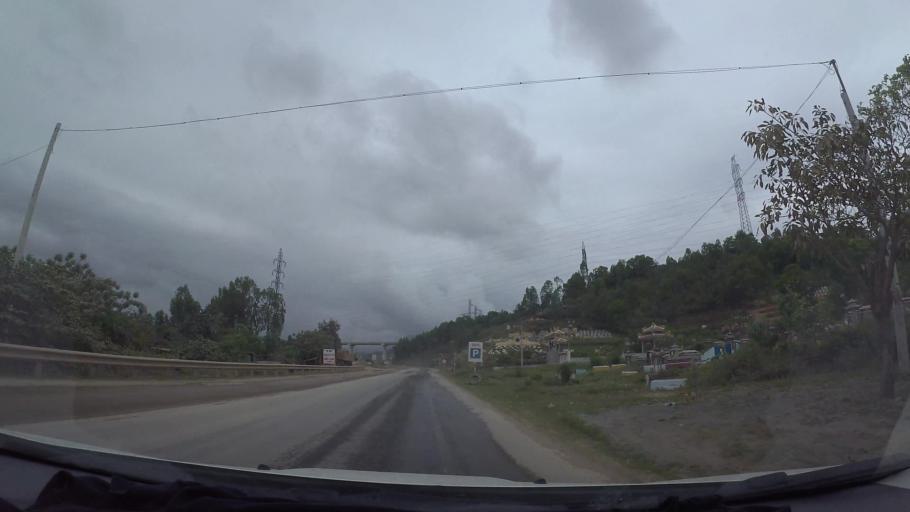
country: VN
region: Da Nang
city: Lien Chieu
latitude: 16.1002
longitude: 108.0931
